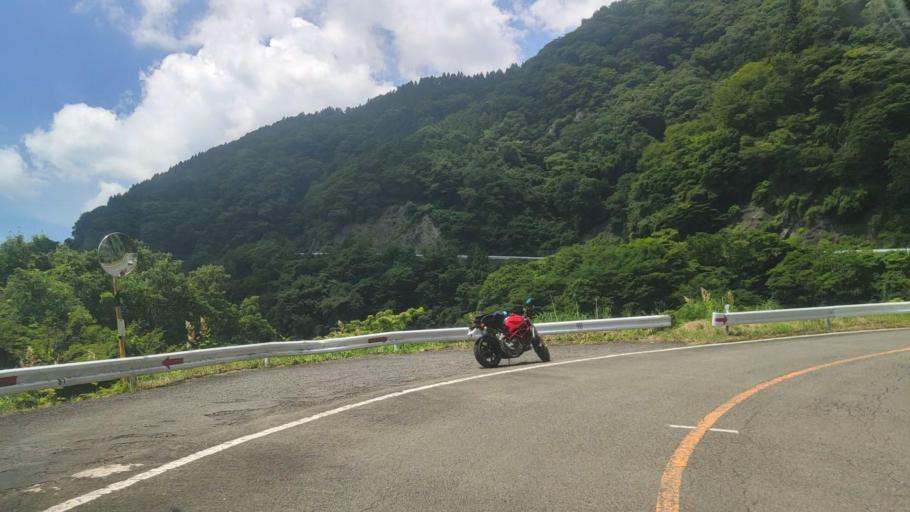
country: JP
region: Gifu
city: Tarui
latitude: 35.3910
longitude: 136.4389
